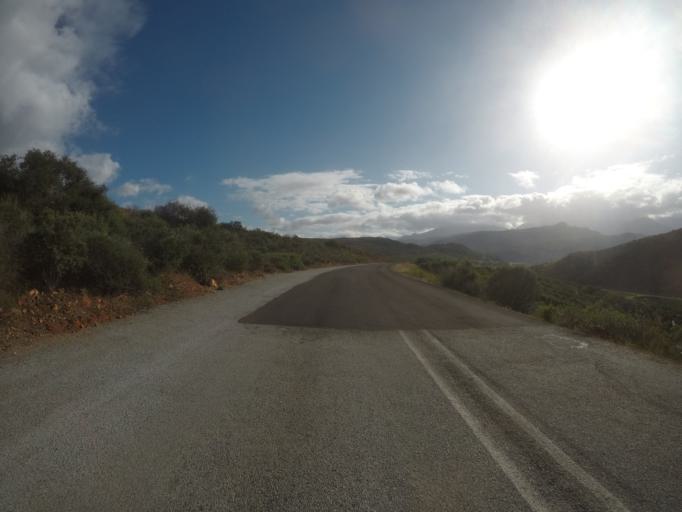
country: ZA
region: Western Cape
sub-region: West Coast District Municipality
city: Clanwilliam
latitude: -32.4349
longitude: 18.9464
